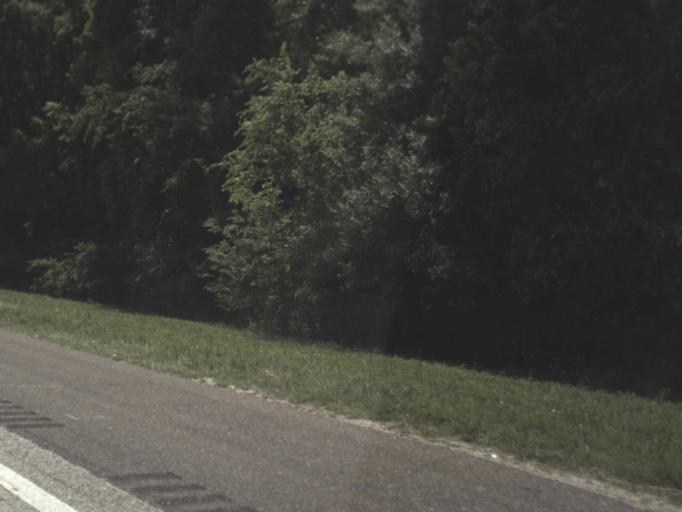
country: US
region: Florida
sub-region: Saint Johns County
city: Fruit Cove
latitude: 30.1447
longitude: -81.5434
